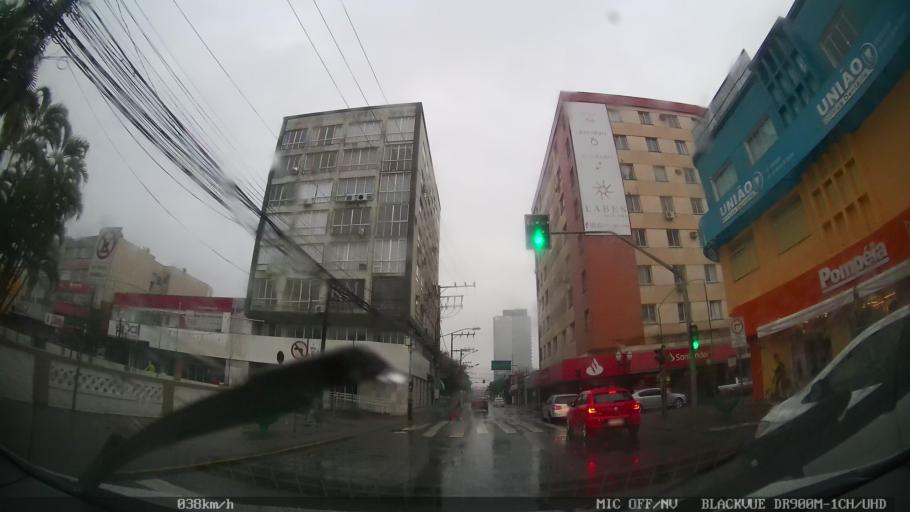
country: BR
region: Santa Catarina
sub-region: Itajai
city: Itajai
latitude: -26.9064
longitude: -48.6594
